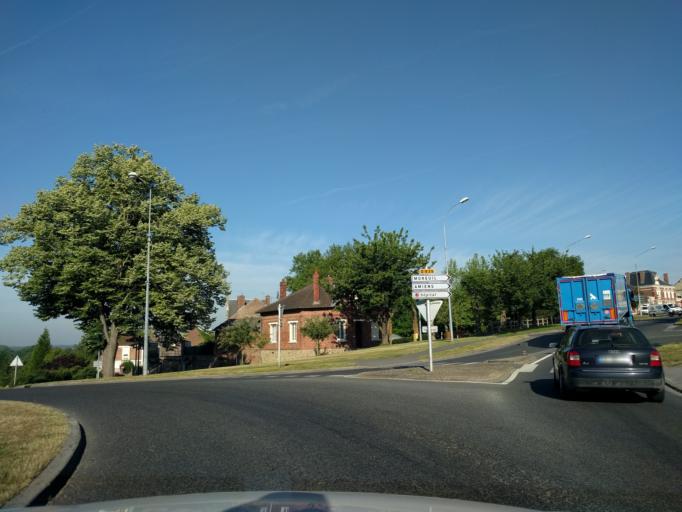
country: FR
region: Picardie
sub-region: Departement de la Somme
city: Montdidier
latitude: 49.6460
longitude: 2.5731
